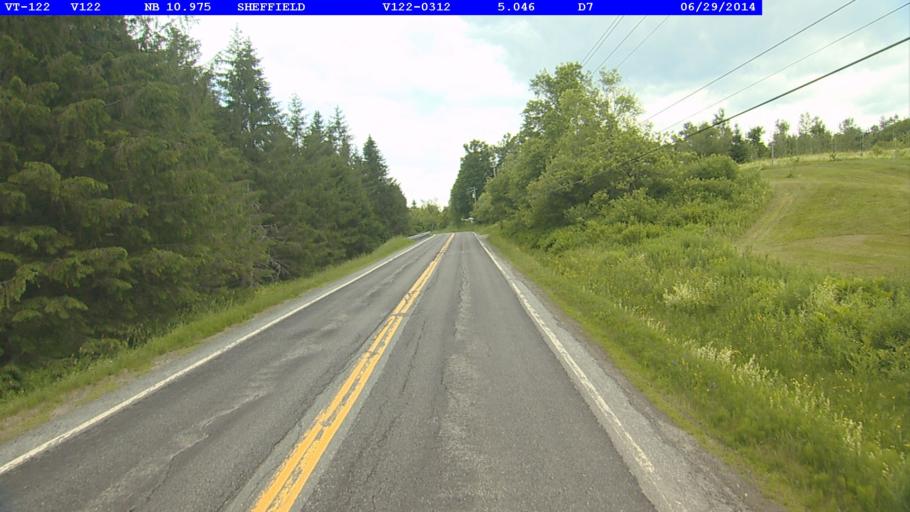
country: US
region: Vermont
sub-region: Caledonia County
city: Lyndonville
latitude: 44.6427
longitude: -72.1548
